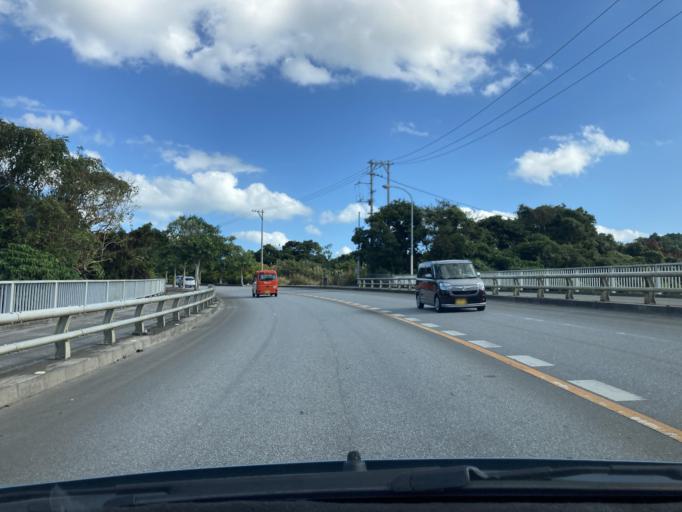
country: JP
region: Okinawa
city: Gushikawa
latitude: 26.3688
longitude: 127.8310
